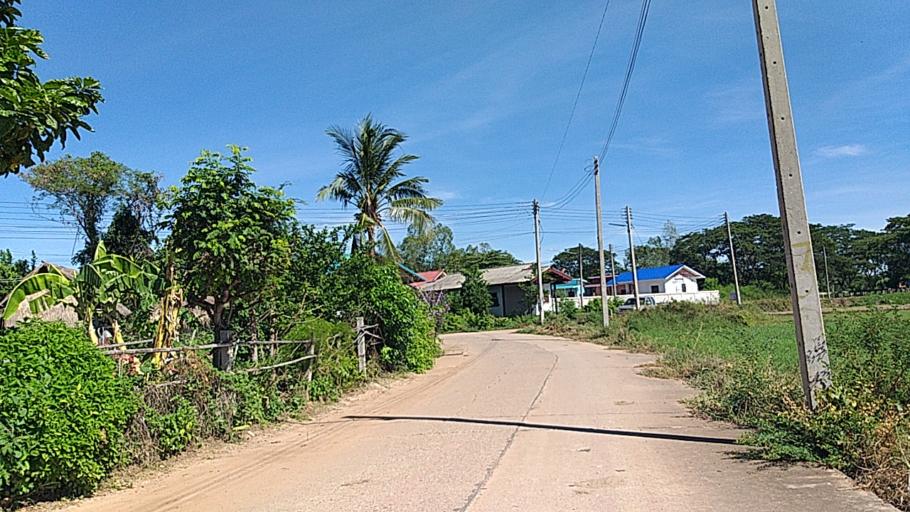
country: TH
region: Chaiyaphum
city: Ban Thaen
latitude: 16.4123
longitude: 102.3546
